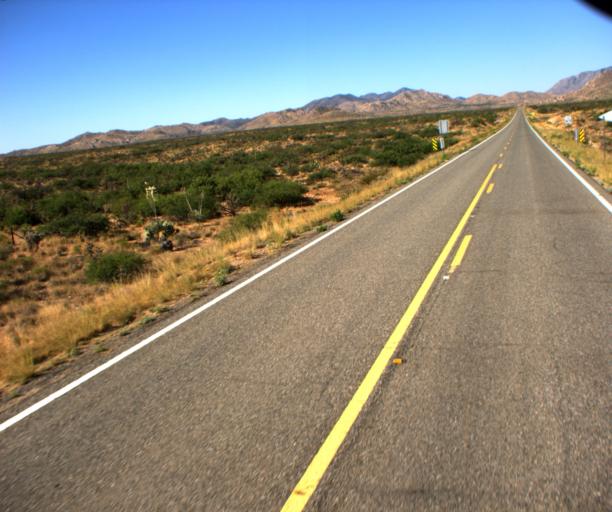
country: US
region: Arizona
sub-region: Graham County
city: Swift Trail Junction
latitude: 32.5958
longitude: -109.6882
